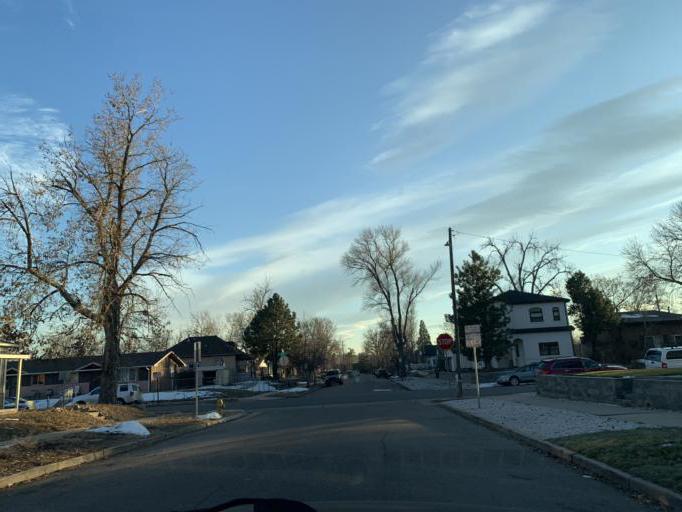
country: US
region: Colorado
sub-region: Adams County
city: Berkley
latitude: 39.7859
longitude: -105.0358
